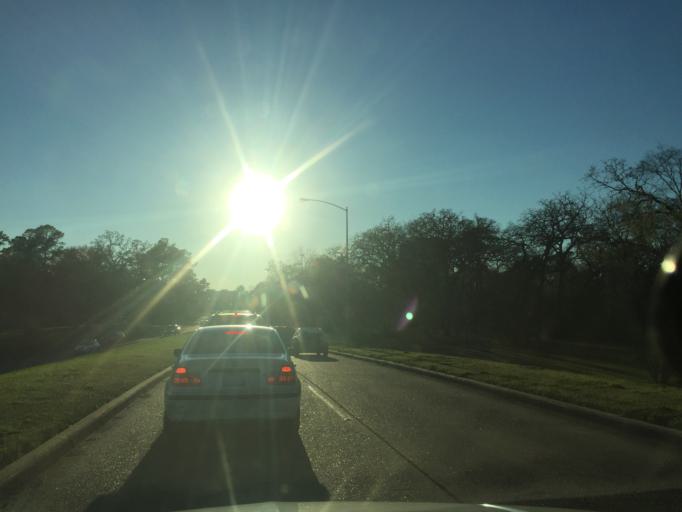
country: US
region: Texas
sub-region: Harris County
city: Hunters Creek Village
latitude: 29.7684
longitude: -95.4507
